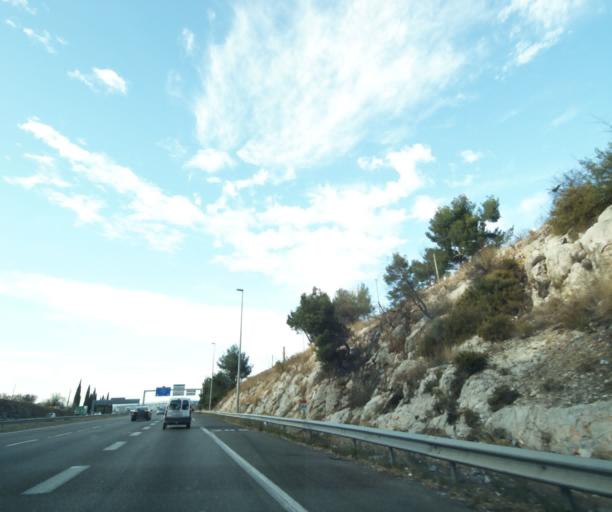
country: FR
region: Provence-Alpes-Cote d'Azur
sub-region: Departement des Bouches-du-Rhone
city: Les Pennes-Mirabeau
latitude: 43.4125
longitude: 5.2819
